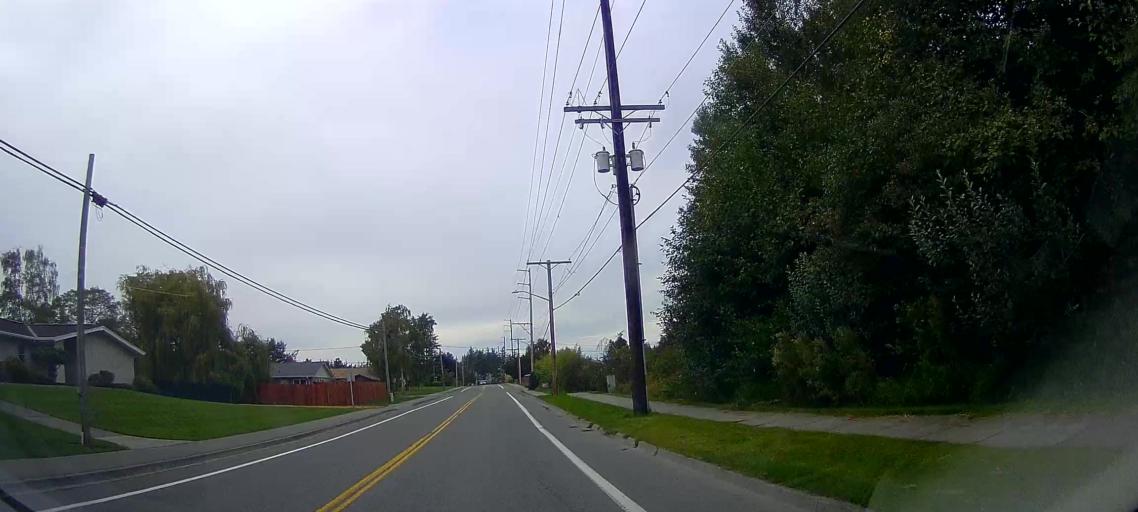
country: US
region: Washington
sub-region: Skagit County
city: Anacortes
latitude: 48.4912
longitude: -122.6252
